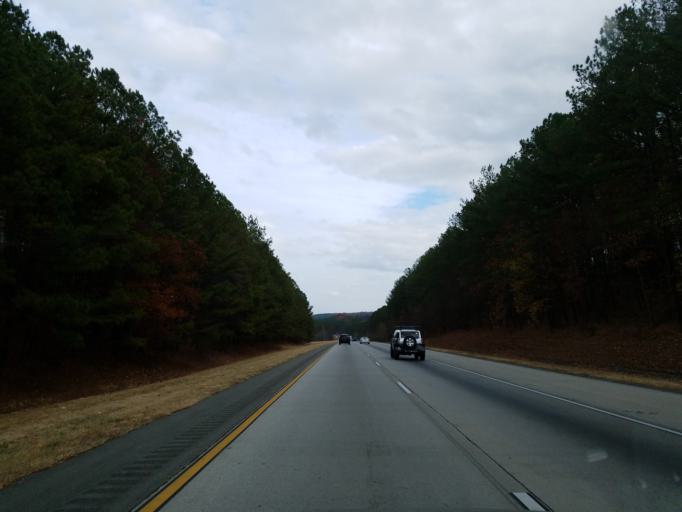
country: US
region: Georgia
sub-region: Carroll County
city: Mount Zion
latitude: 33.6872
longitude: -85.2363
